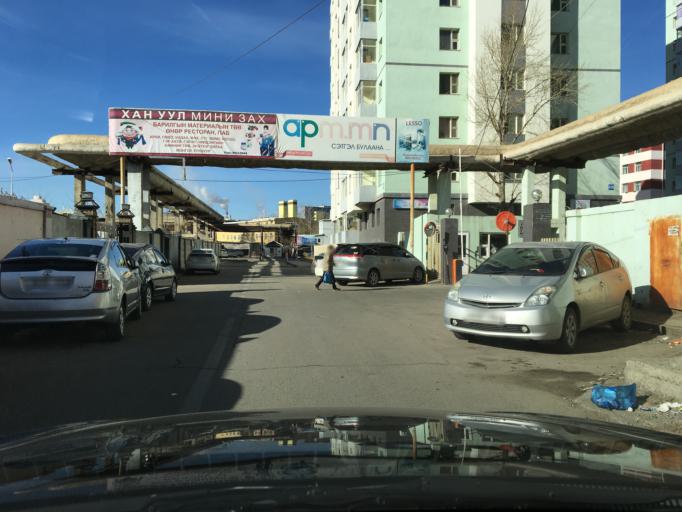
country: MN
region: Ulaanbaatar
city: Ulaanbaatar
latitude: 47.8958
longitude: 106.8945
